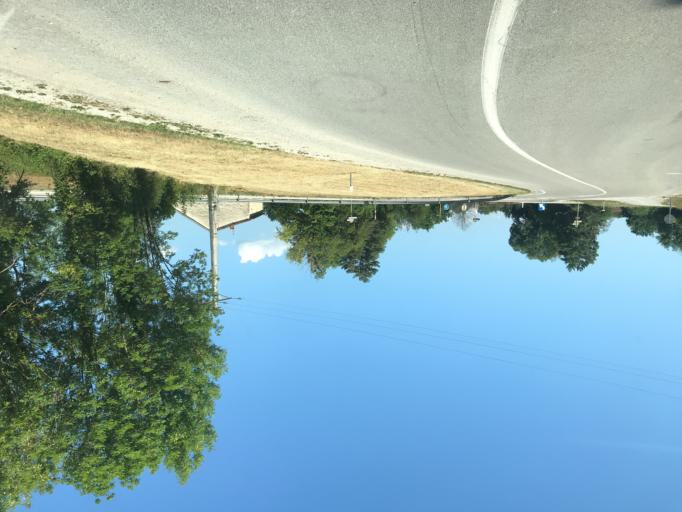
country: FR
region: Franche-Comte
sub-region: Departement du Jura
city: Moirans-en-Montagne
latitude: 46.4666
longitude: 5.7164
